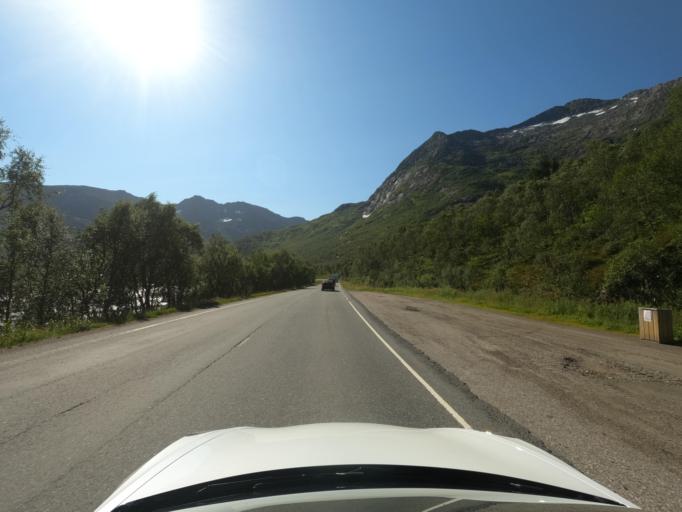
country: NO
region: Nordland
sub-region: Lodingen
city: Lodingen
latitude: 68.5350
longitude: 15.7231
